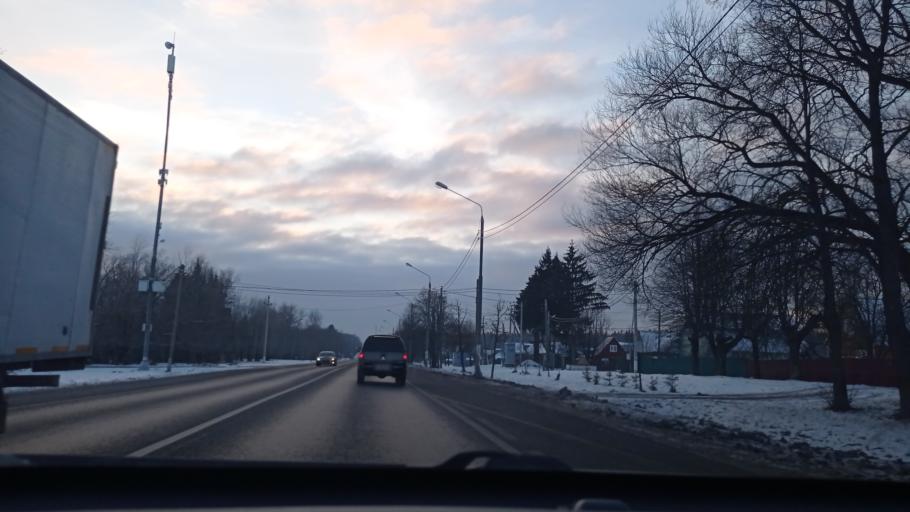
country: RU
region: Moskovskaya
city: Selyatino
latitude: 55.2614
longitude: 37.1017
